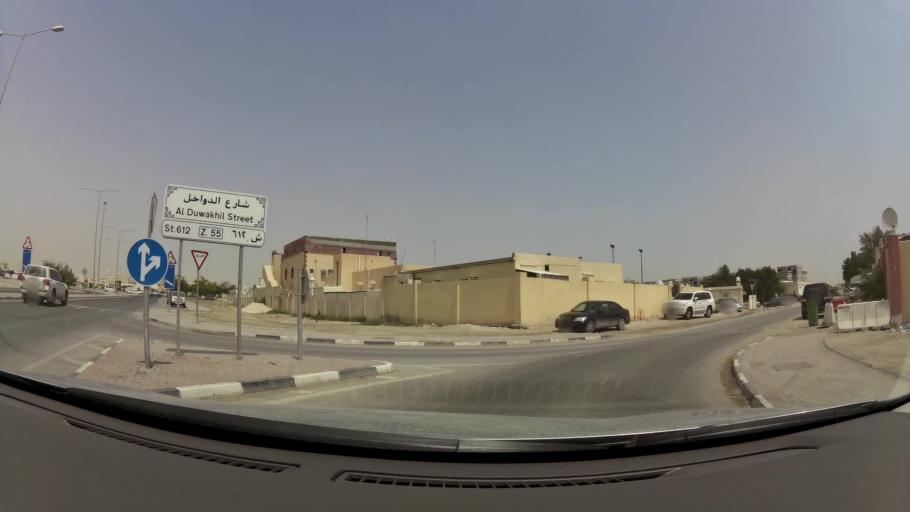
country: QA
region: Baladiyat ar Rayyan
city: Ar Rayyan
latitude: 25.2446
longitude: 51.4205
